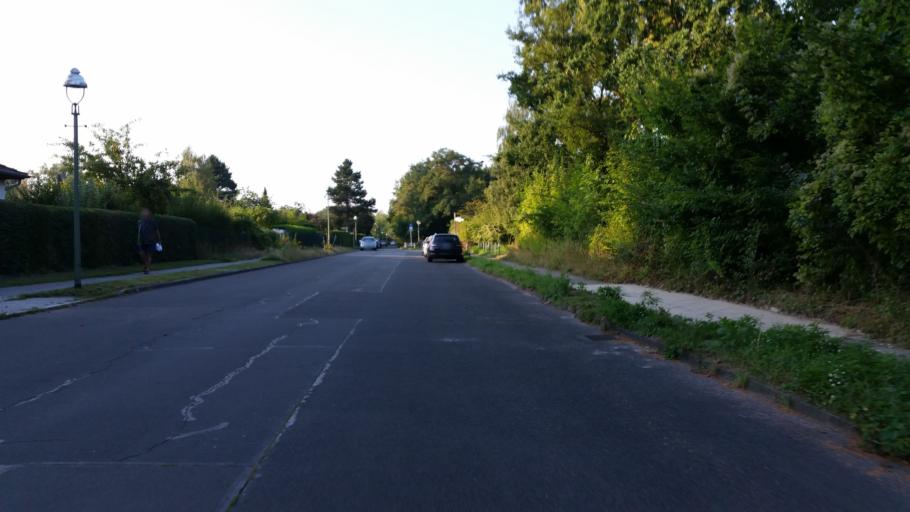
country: DE
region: Berlin
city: Lichtenrade
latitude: 52.4016
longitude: 13.3900
